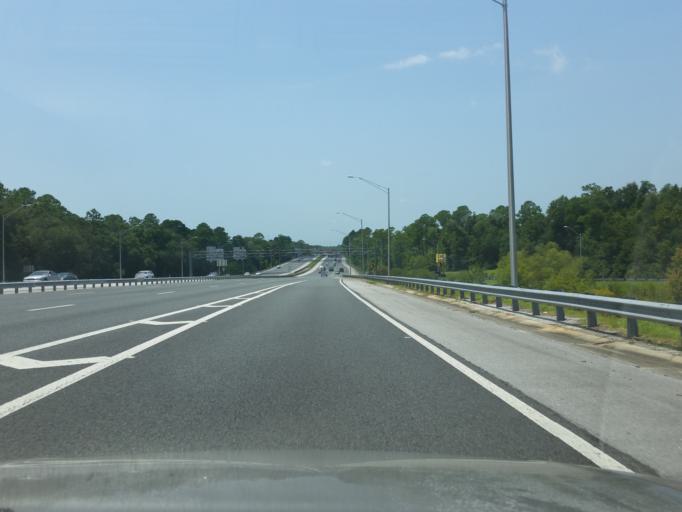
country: US
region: Florida
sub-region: Escambia County
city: Ferry Pass
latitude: 30.5037
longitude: -87.2344
